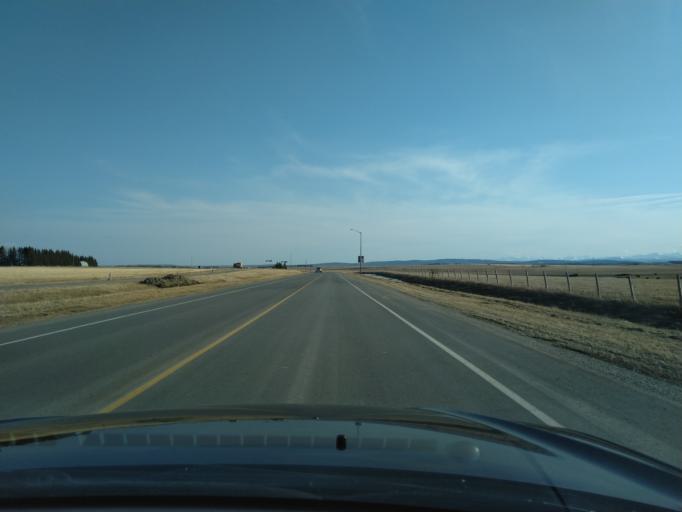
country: CA
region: Alberta
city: Cochrane
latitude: 51.0997
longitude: -114.3888
